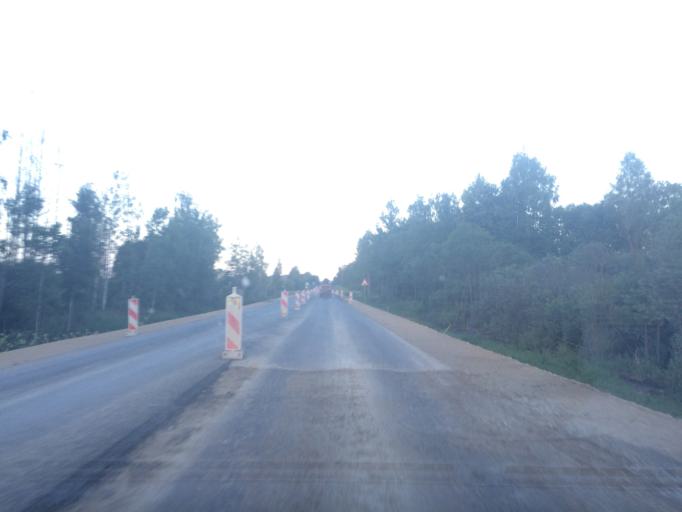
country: LT
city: Zarasai
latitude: 55.7505
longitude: 26.3184
